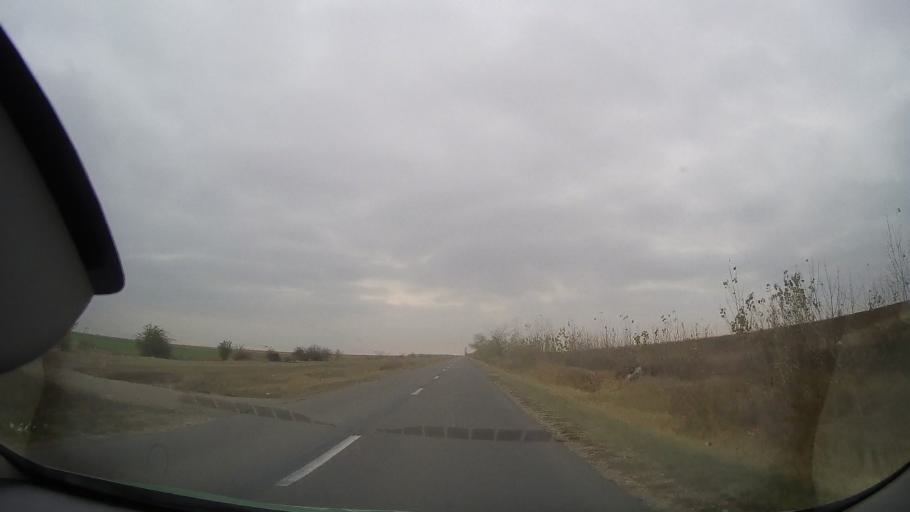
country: RO
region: Ialomita
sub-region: Comuna Garbovi
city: Garbovi
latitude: 44.7713
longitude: 26.7443
